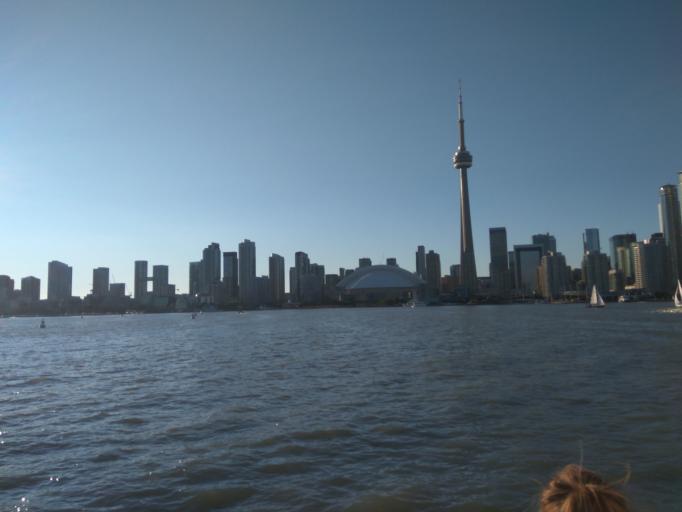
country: CA
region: Ontario
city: Toronto
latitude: 43.6313
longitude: -79.3824
